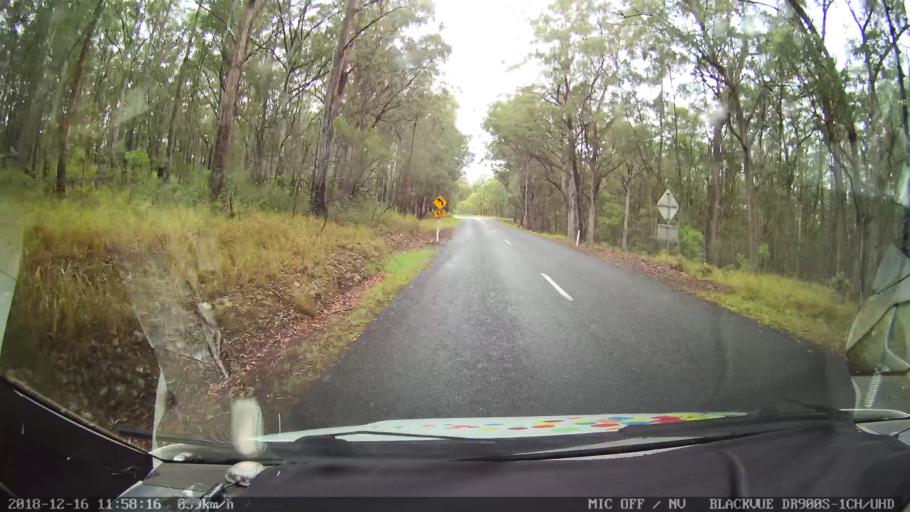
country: AU
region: New South Wales
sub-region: Tenterfield Municipality
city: Carrolls Creek
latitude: -28.9210
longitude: 152.3130
